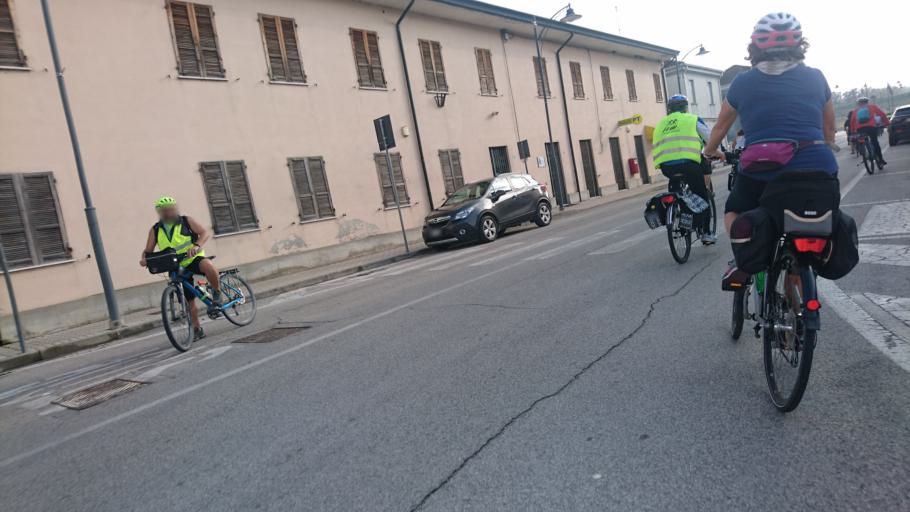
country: IT
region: Veneto
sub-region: Provincia di Rovigo
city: Polesella
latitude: 44.9625
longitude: 11.7551
